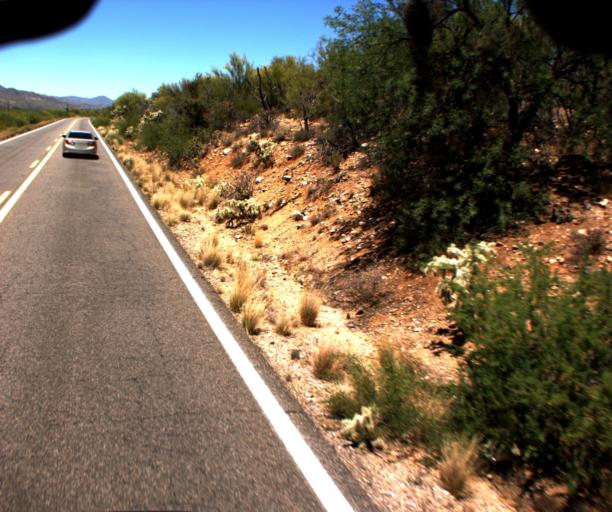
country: US
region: Arizona
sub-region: Pinal County
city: Kearny
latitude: 33.1105
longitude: -110.7650
